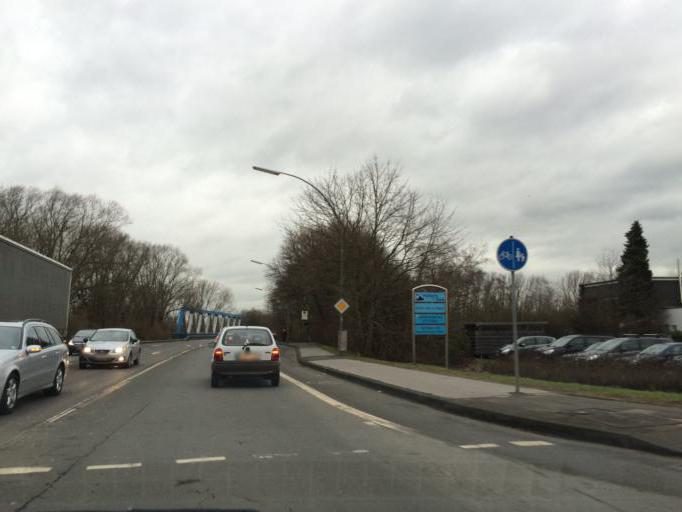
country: DE
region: North Rhine-Westphalia
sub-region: Regierungsbezirk Munster
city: Haltern
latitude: 51.7277
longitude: 7.1865
